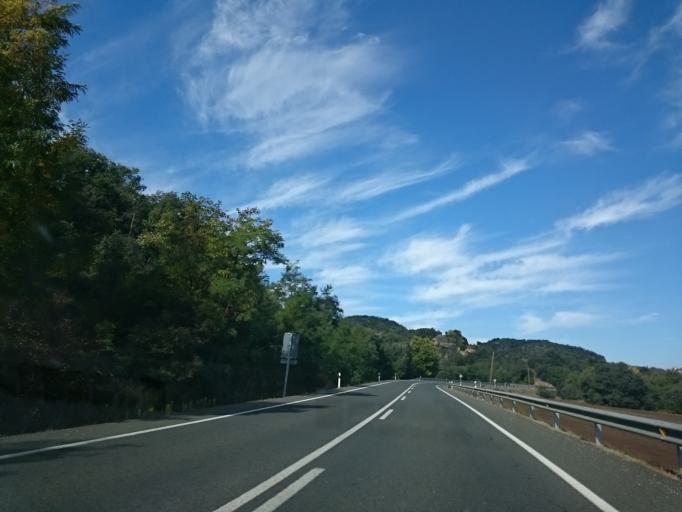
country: ES
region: Aragon
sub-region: Provincia de Huesca
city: Benavarri / Benabarre
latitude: 42.0880
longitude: 0.4933
